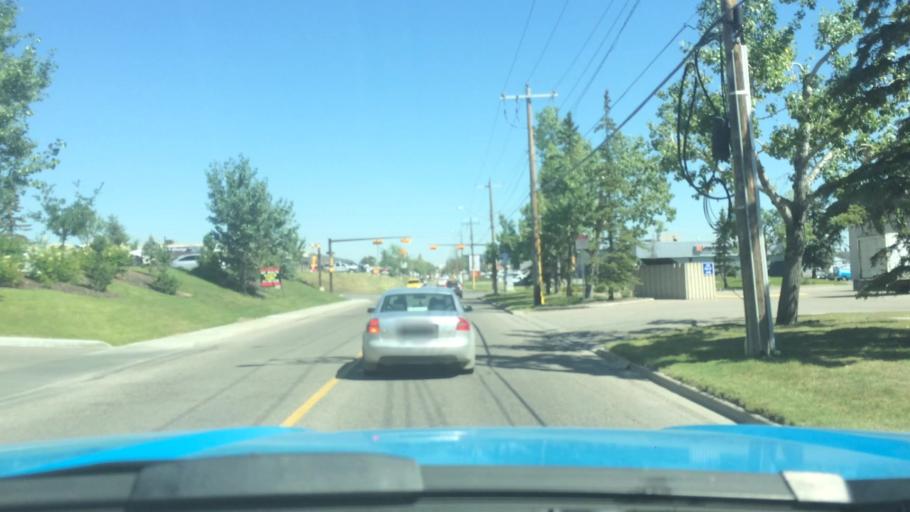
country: CA
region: Alberta
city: Calgary
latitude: 51.0562
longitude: -113.9860
